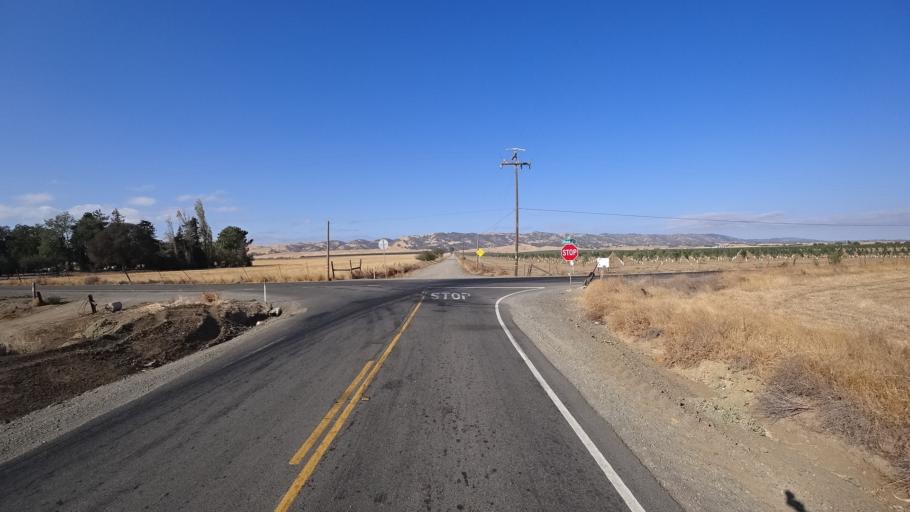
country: US
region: California
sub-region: Yolo County
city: Esparto
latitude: 38.7811
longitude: -122.0435
